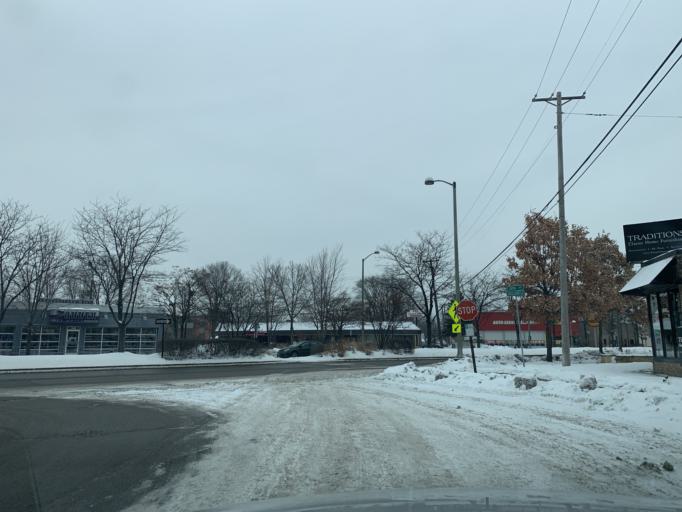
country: US
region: Minnesota
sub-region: Hennepin County
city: Saint Louis Park
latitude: 44.9361
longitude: -93.3341
